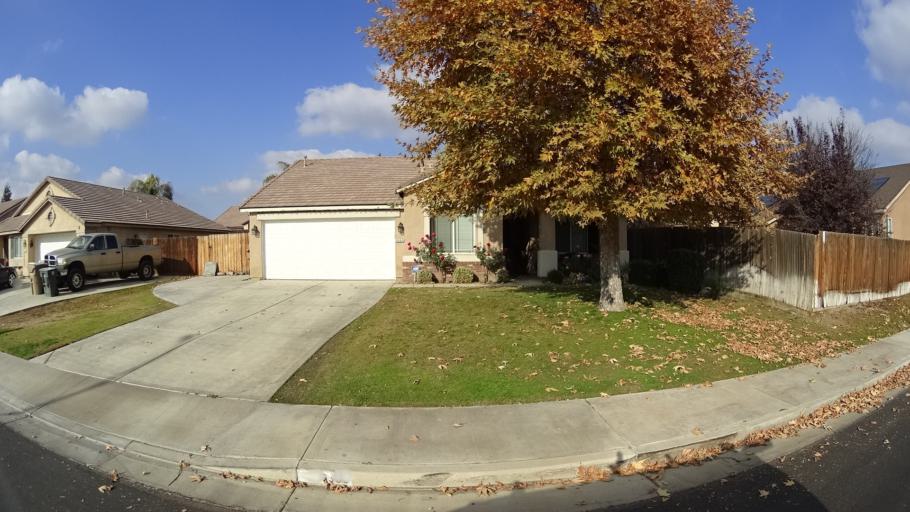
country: US
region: California
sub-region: Kern County
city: Greenacres
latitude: 35.3059
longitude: -119.1055
